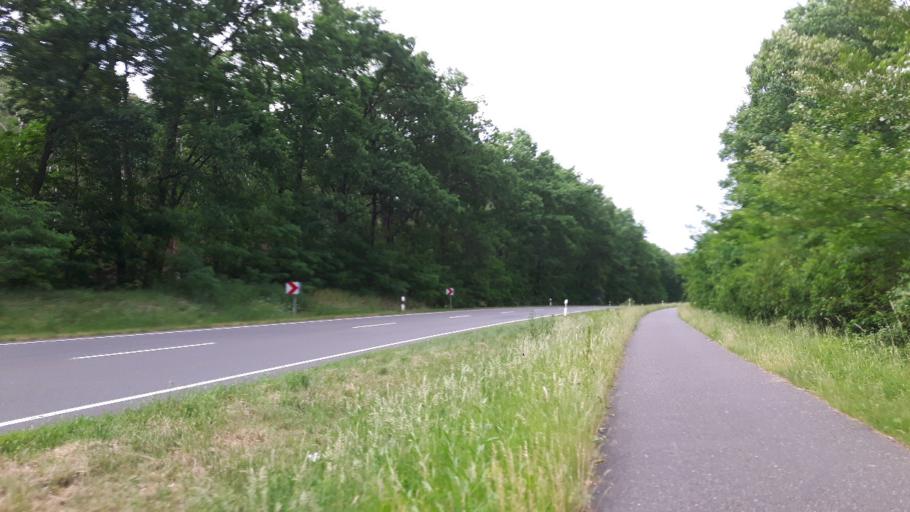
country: DE
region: Brandenburg
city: Michendorf
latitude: 52.3312
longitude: 13.0394
